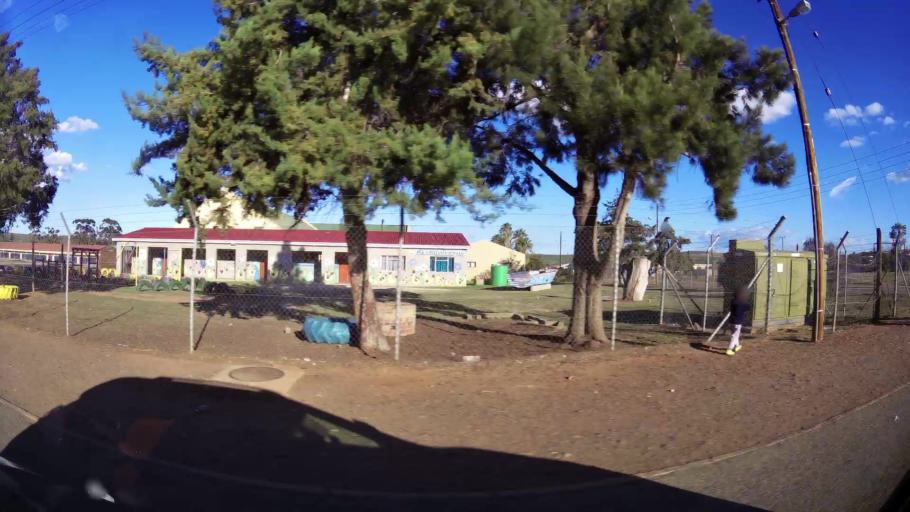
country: ZA
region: Western Cape
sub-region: Eden District Municipality
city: Riversdale
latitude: -34.1030
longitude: 20.9613
